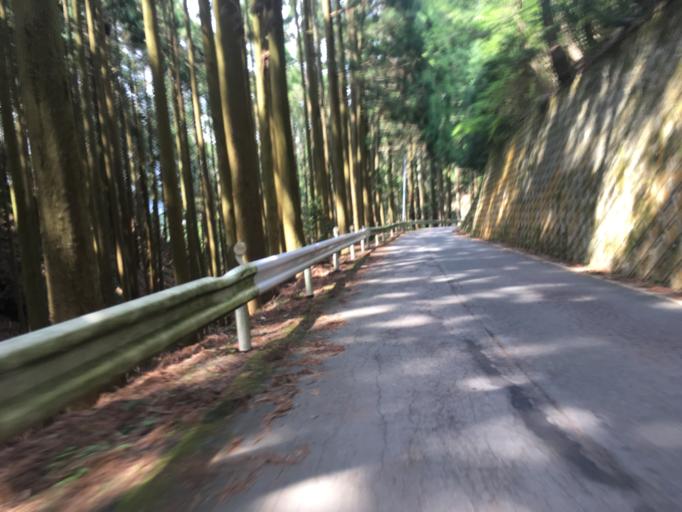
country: JP
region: Kyoto
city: Kameoka
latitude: 35.0659
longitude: 135.6120
